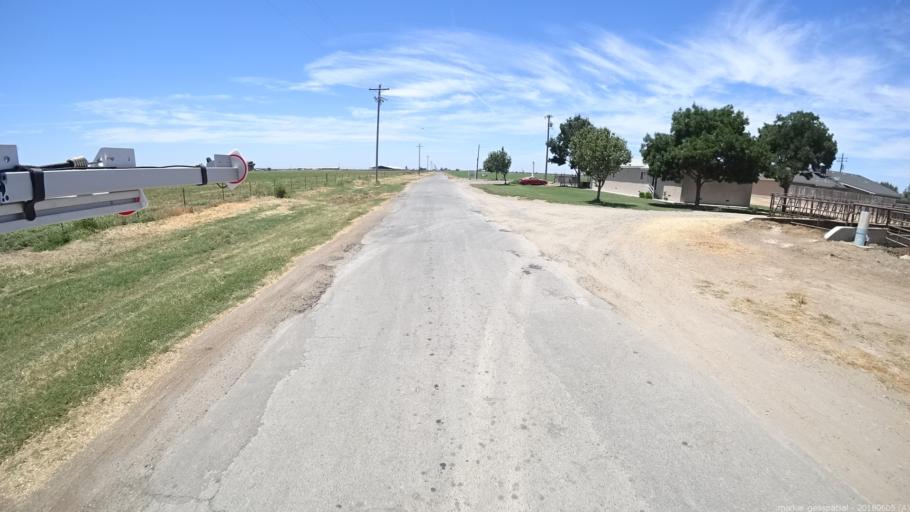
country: US
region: California
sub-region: Madera County
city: Chowchilla
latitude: 37.0982
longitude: -120.3206
